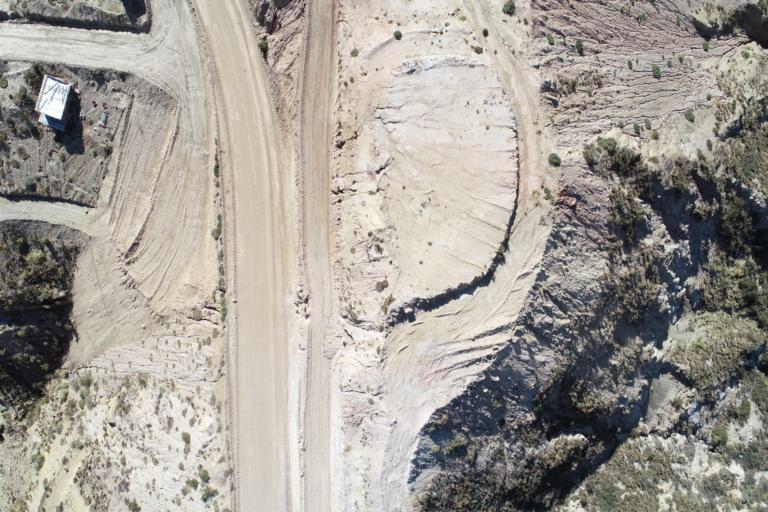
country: BO
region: La Paz
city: La Paz
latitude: -16.5492
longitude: -68.1082
